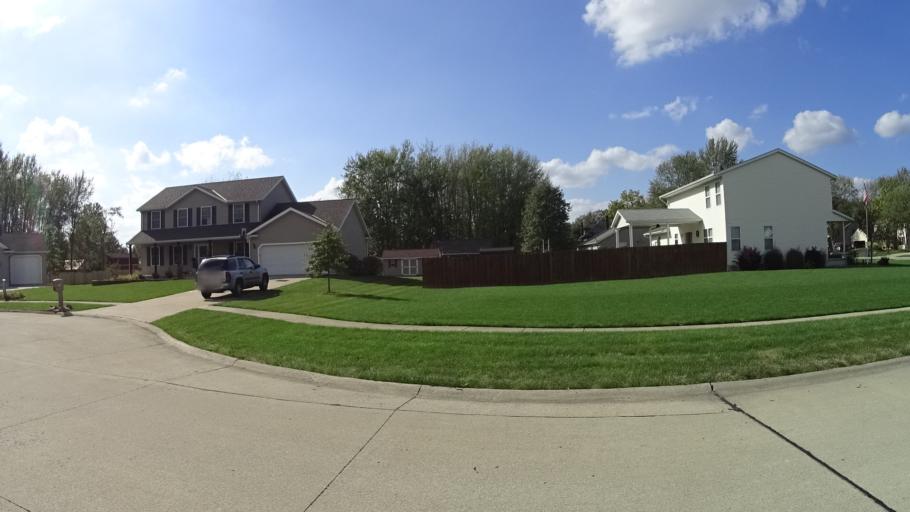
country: US
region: Ohio
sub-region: Lorain County
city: Grafton
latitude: 41.2738
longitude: -82.0496
